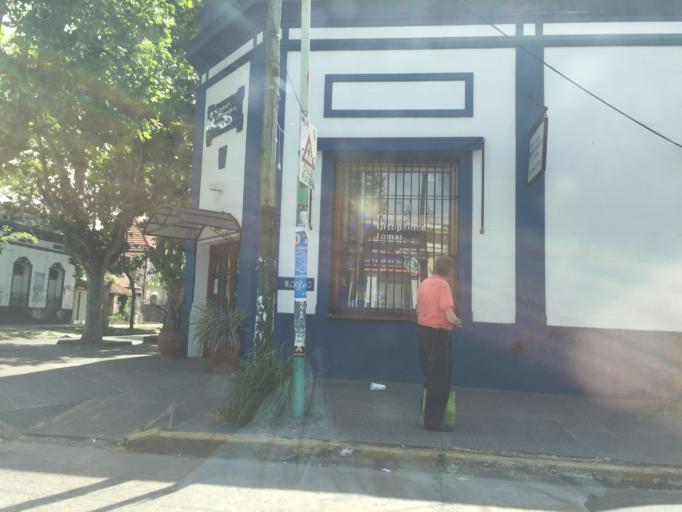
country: AR
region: Buenos Aires
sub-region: Partido de Lomas de Zamora
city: Lomas de Zamora
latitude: -34.7553
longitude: -58.4031
